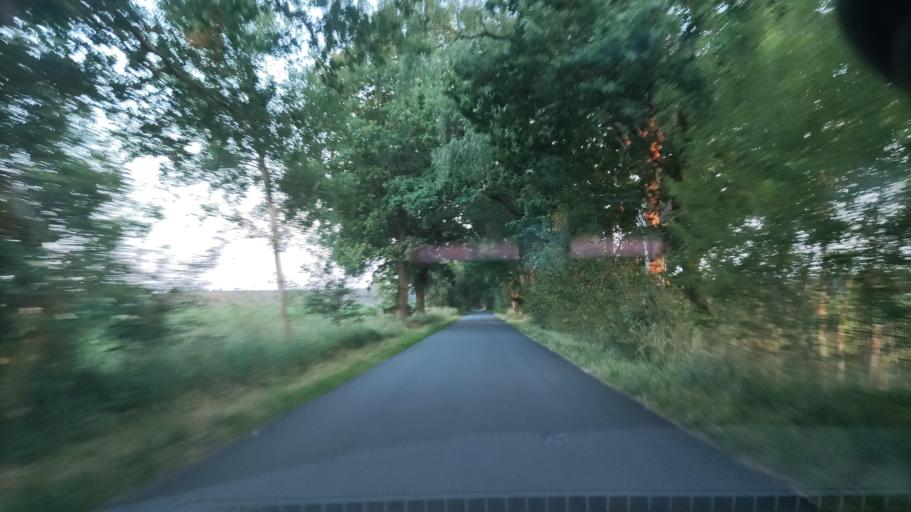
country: DE
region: Lower Saxony
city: Egestorf
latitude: 53.1364
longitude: 10.0396
